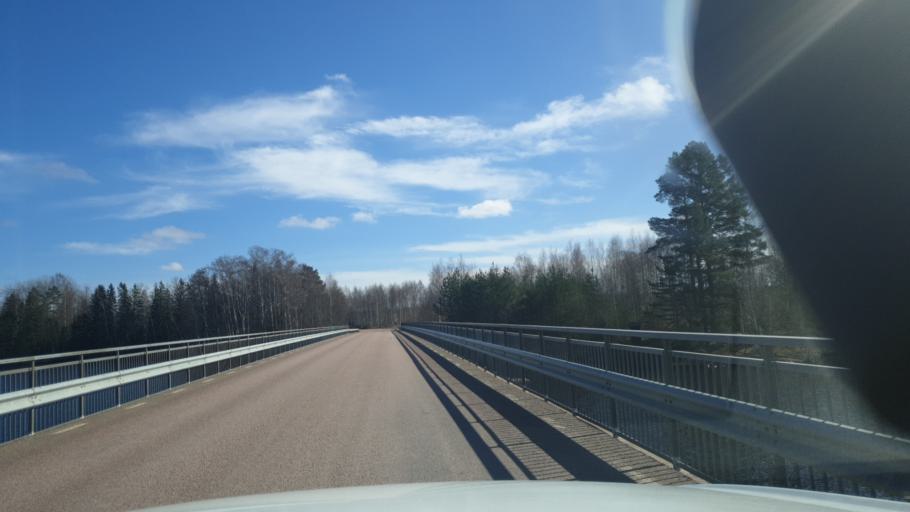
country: SE
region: Vaermland
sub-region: Arvika Kommun
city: Arvika
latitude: 59.6993
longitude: 12.4817
